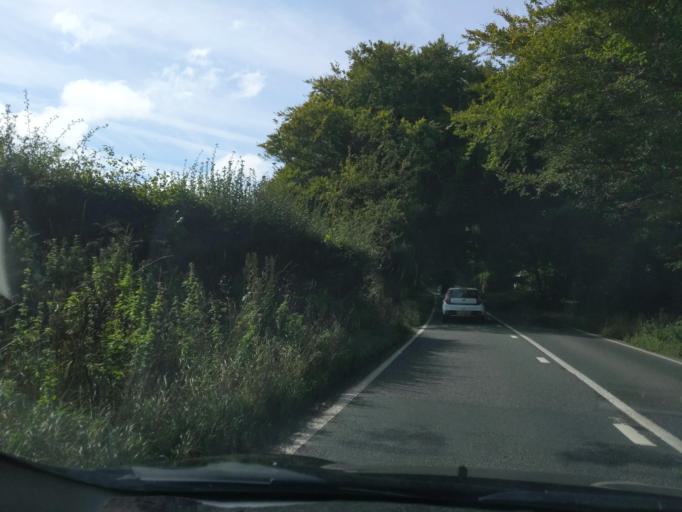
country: GB
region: England
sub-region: Cornwall
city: Camelford
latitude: 50.6573
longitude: -4.6028
